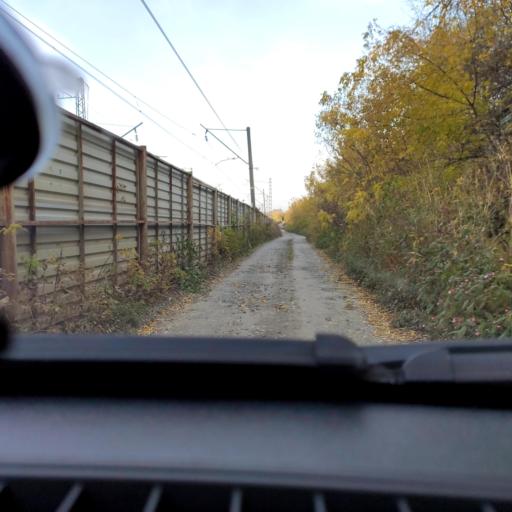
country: RU
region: Bashkortostan
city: Ufa
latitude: 54.7397
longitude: 55.9280
